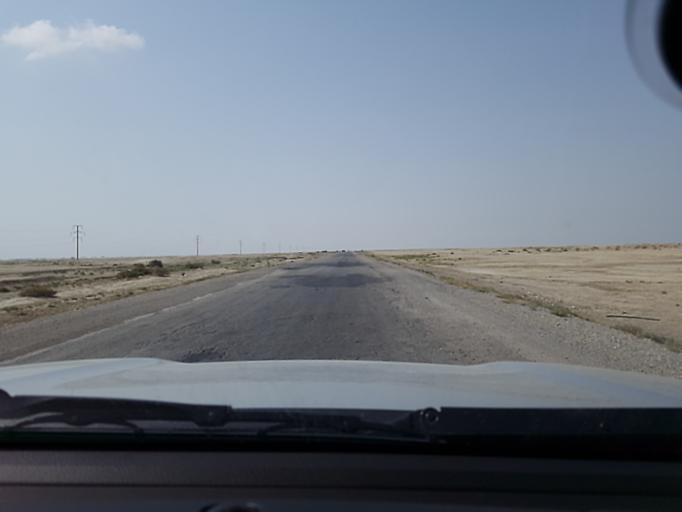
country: TM
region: Balkan
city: Gumdag
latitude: 38.8926
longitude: 54.5928
